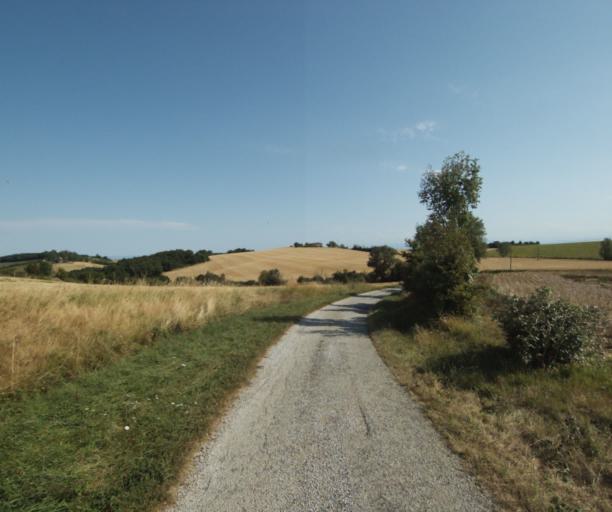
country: FR
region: Midi-Pyrenees
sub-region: Departement de la Haute-Garonne
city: Avignonet-Lauragais
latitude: 43.4199
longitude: 1.8167
